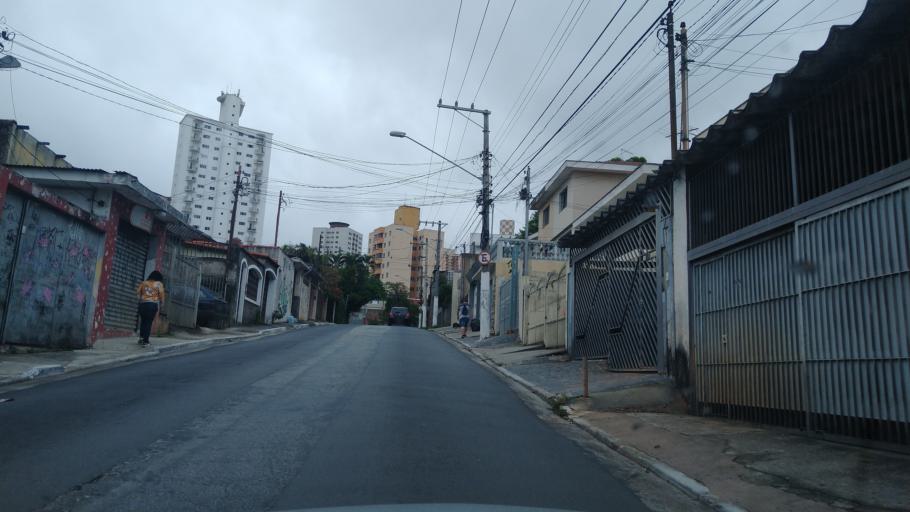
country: BR
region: Sao Paulo
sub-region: Sao Paulo
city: Sao Paulo
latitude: -23.4756
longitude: -46.6380
